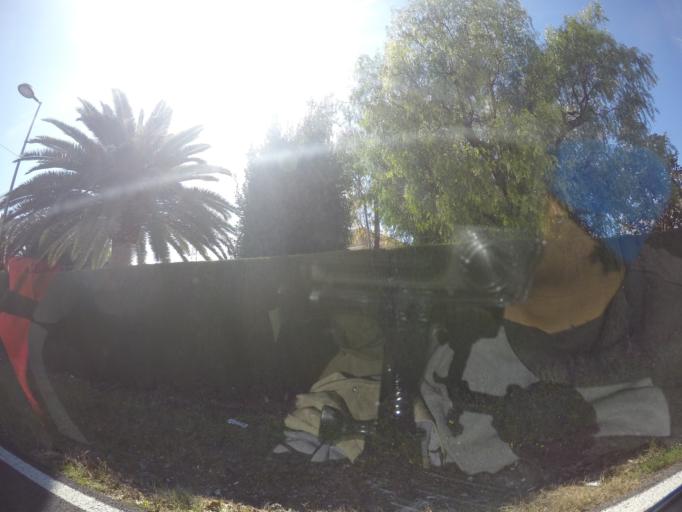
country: ES
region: Catalonia
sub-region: Provincia de Tarragona
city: Sant Jaume dels Domenys
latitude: 41.2806
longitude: 1.5497
